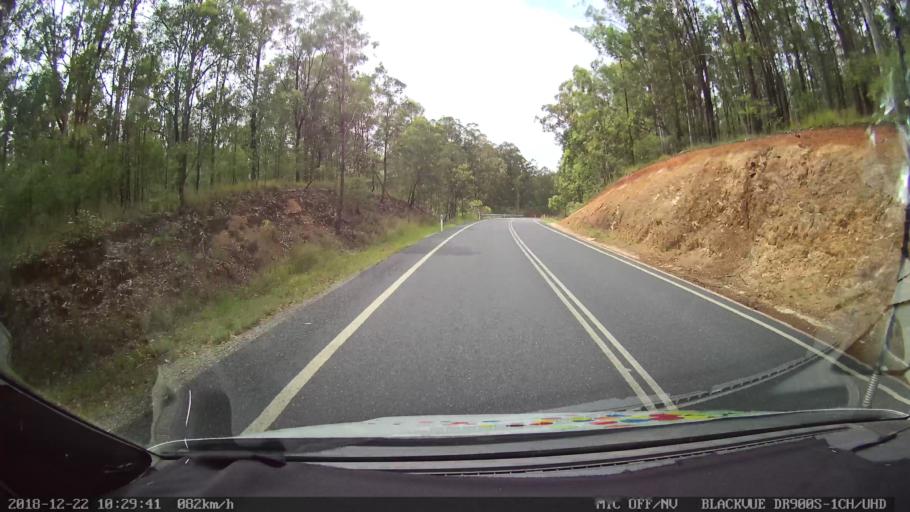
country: AU
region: New South Wales
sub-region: Clarence Valley
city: Gordon
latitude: -29.6127
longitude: 152.6071
